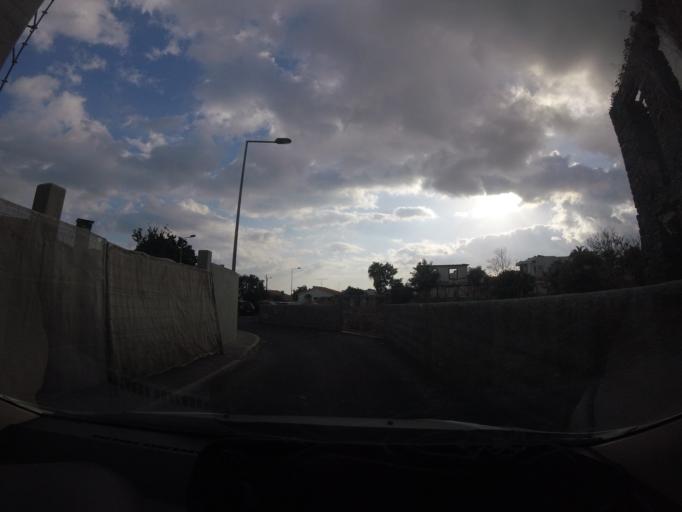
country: PT
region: Madeira
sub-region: Funchal
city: Nossa Senhora do Monte
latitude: 32.6546
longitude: -16.9165
